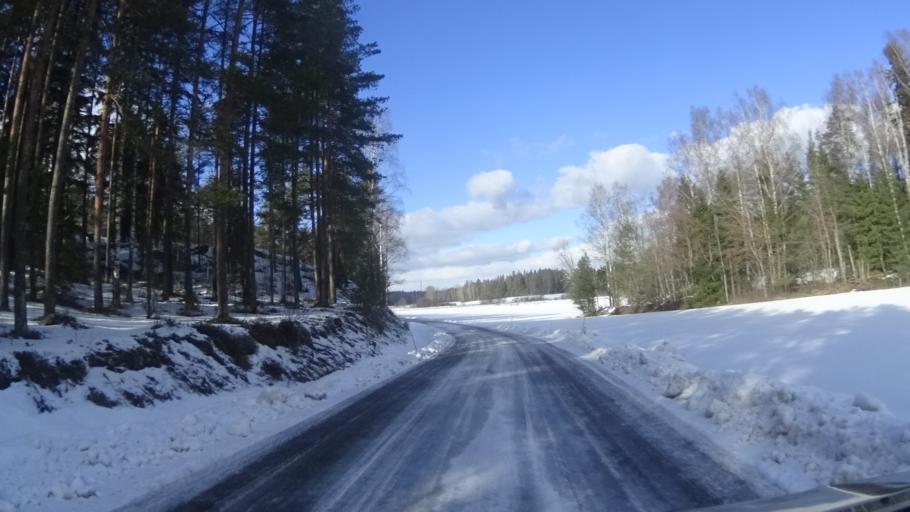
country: FI
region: Uusimaa
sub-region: Helsinki
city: Vantaa
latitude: 60.2401
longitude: 25.1808
